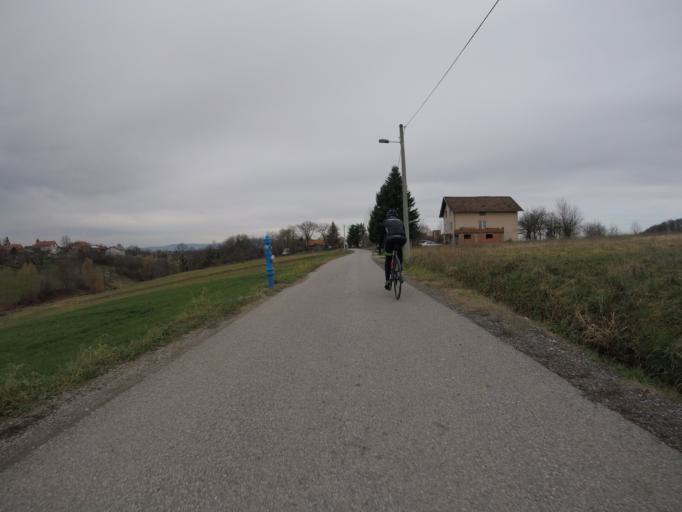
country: HR
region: Grad Zagreb
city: Strmec
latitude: 45.6624
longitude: 15.8729
